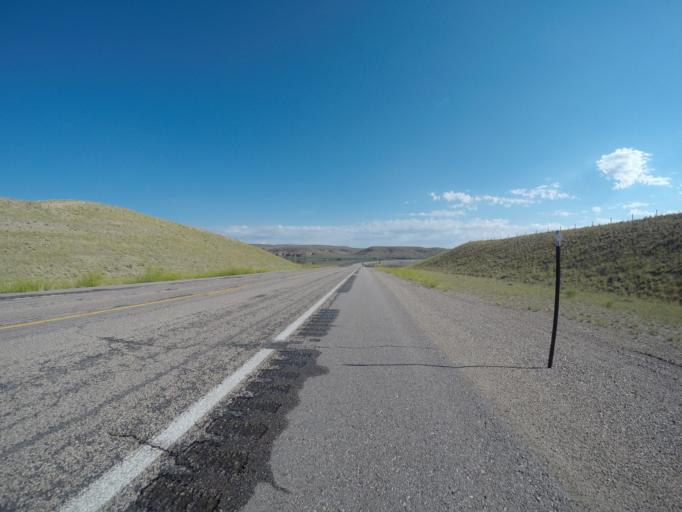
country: US
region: Wyoming
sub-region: Lincoln County
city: Kemmerer
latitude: 42.0790
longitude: -110.1604
